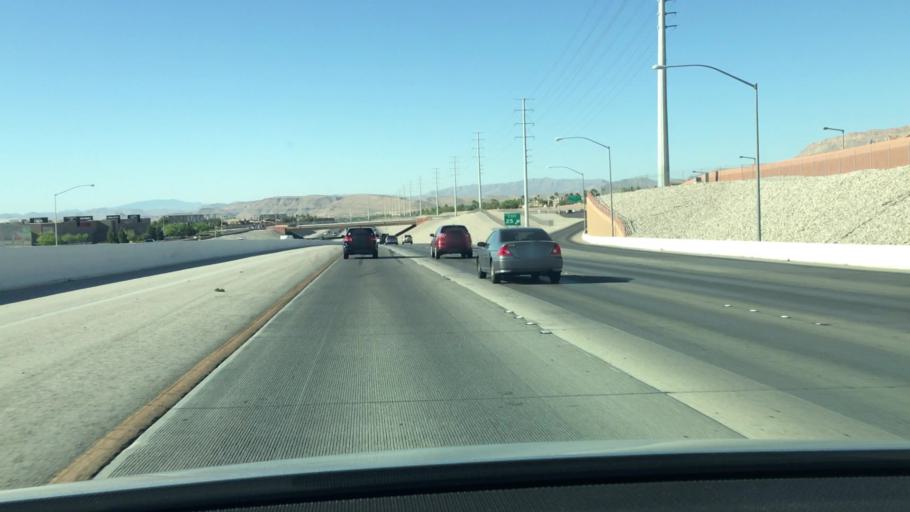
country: US
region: Nevada
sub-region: Clark County
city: Summerlin South
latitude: 36.1492
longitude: -115.3370
